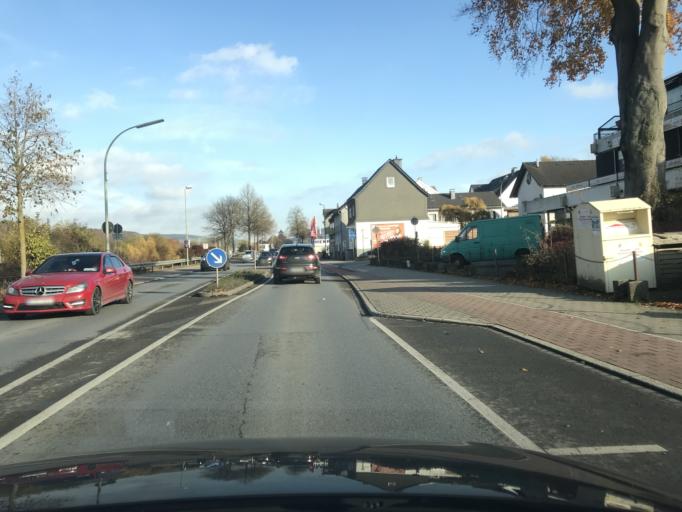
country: DE
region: North Rhine-Westphalia
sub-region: Regierungsbezirk Arnsberg
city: Bestwig
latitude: 51.3605
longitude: 8.3935
